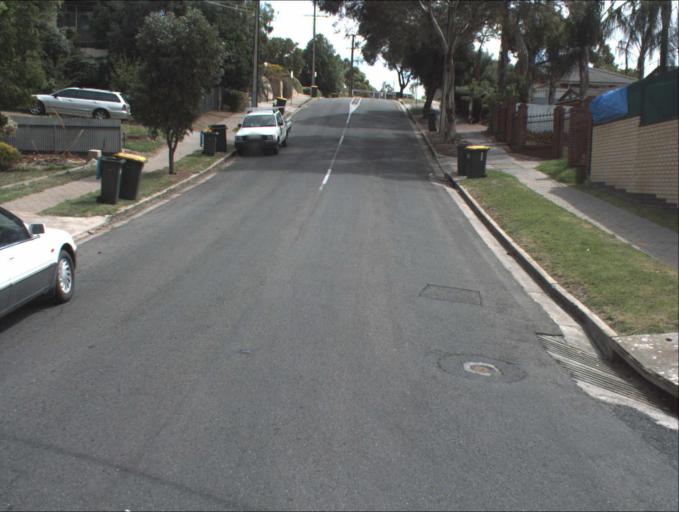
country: AU
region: South Australia
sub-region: Campbelltown
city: Paradise
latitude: -34.8629
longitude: 138.6625
